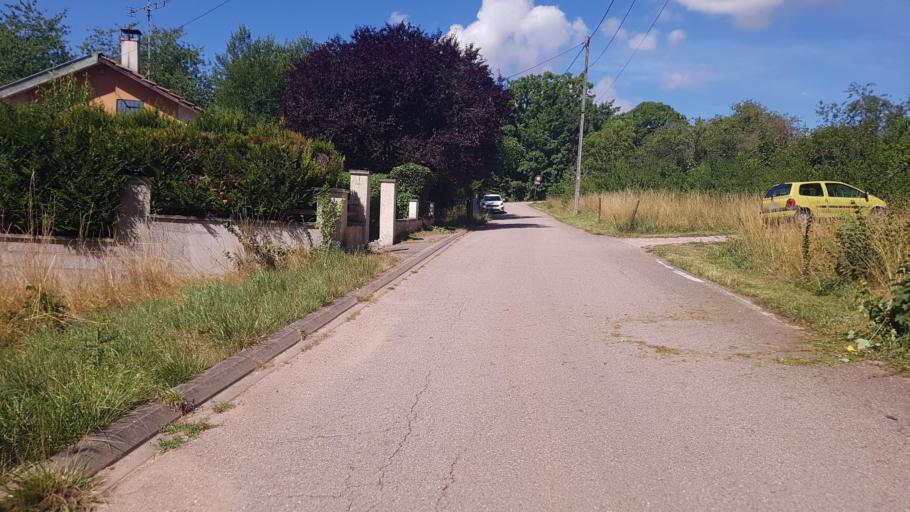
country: FR
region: Lorraine
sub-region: Departement de Meurthe-et-Moselle
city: Dombasle-sur-Meurthe
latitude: 48.6335
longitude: 6.3670
